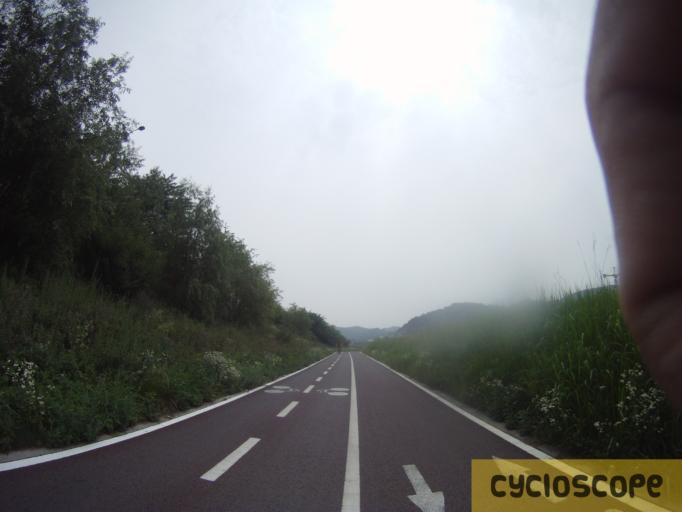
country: KR
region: Gyeonggi-do
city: Anyang-si
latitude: 37.4206
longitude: 126.8977
